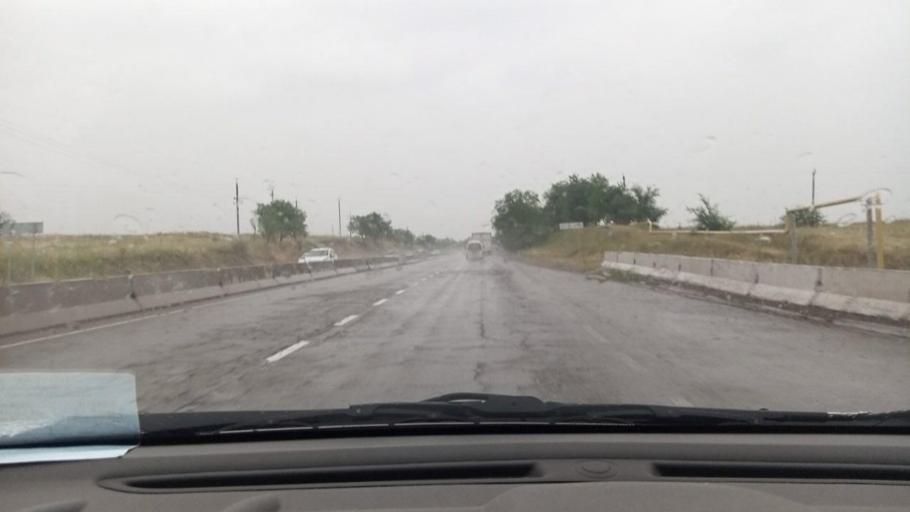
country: UZ
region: Toshkent
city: Angren
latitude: 40.9623
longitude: 69.9473
